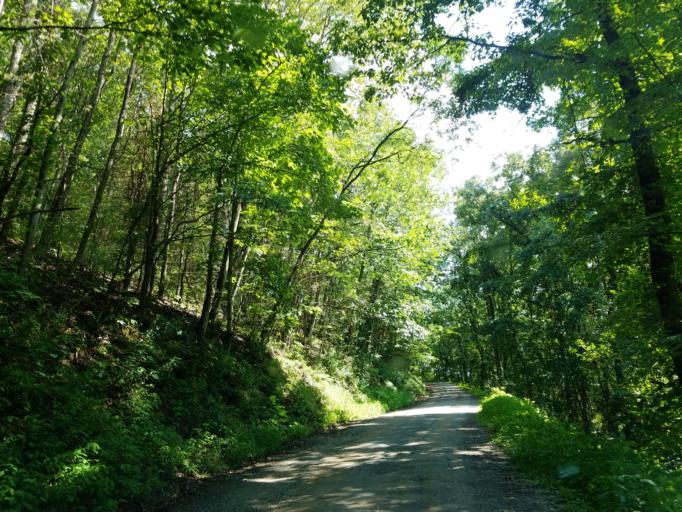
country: US
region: Georgia
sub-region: Fannin County
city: Blue Ridge
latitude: 34.6792
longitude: -84.2491
